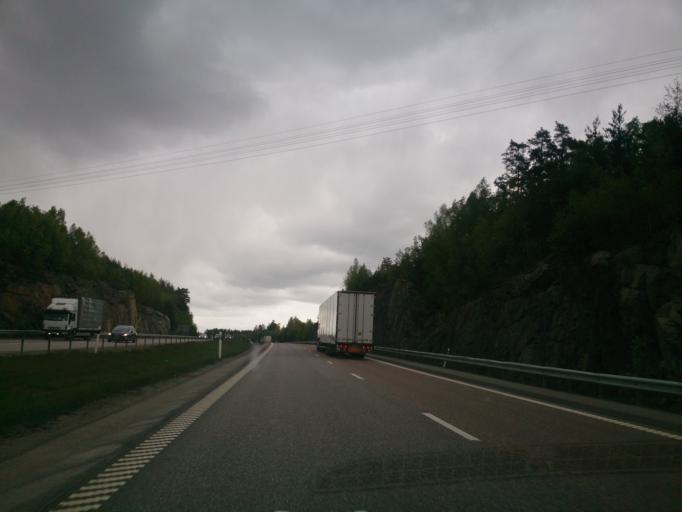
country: SE
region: Soedermanland
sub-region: Trosa Kommun
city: Vagnharad
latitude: 59.0178
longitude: 17.5509
